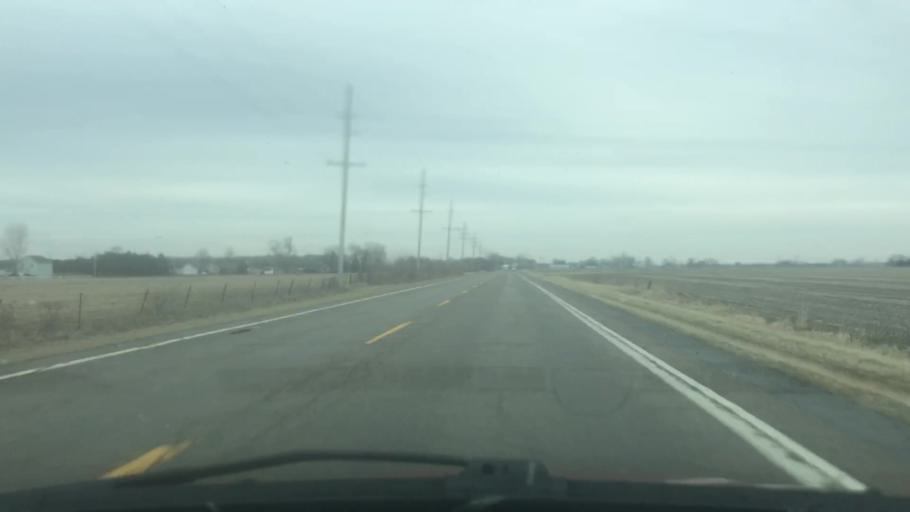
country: US
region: Indiana
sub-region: Porter County
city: Kouts
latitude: 41.3450
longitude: -87.0266
